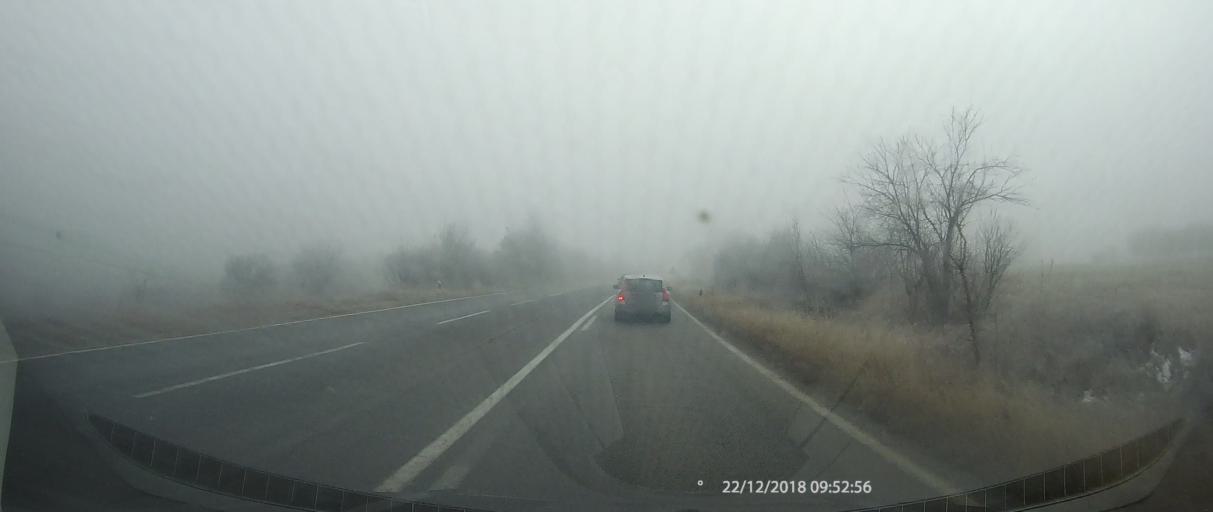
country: MK
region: Staro Nagoricane
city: Staro Nagorichane
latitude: 42.1669
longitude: 21.8334
